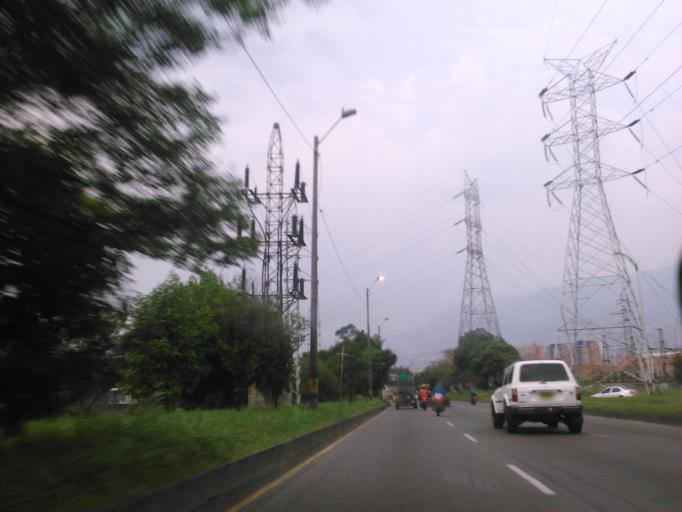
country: CO
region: Antioquia
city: Envigado
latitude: 6.1755
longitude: -75.5952
